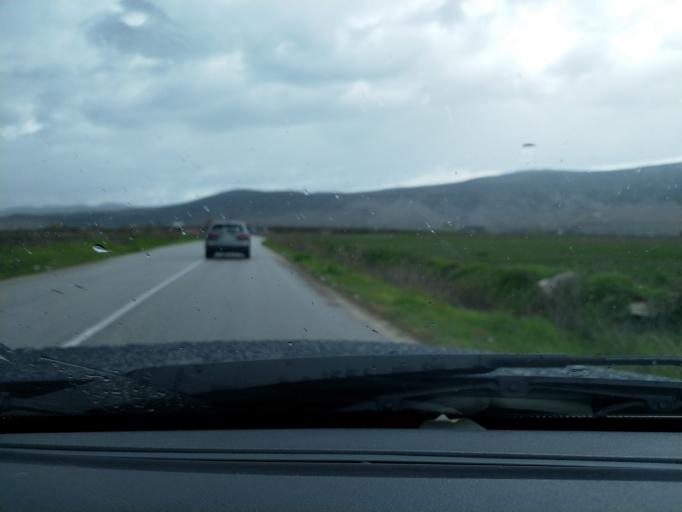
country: GR
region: Thessaly
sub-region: Trikala
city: Taxiarches
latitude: 39.5571
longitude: 21.8902
